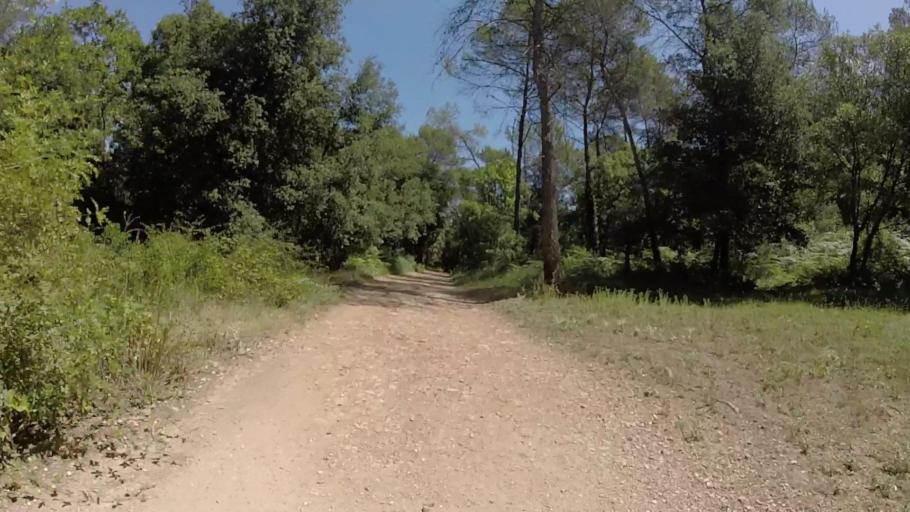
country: FR
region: Provence-Alpes-Cote d'Azur
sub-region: Departement des Alpes-Maritimes
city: Le Cannet
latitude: 43.5980
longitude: 7.0281
